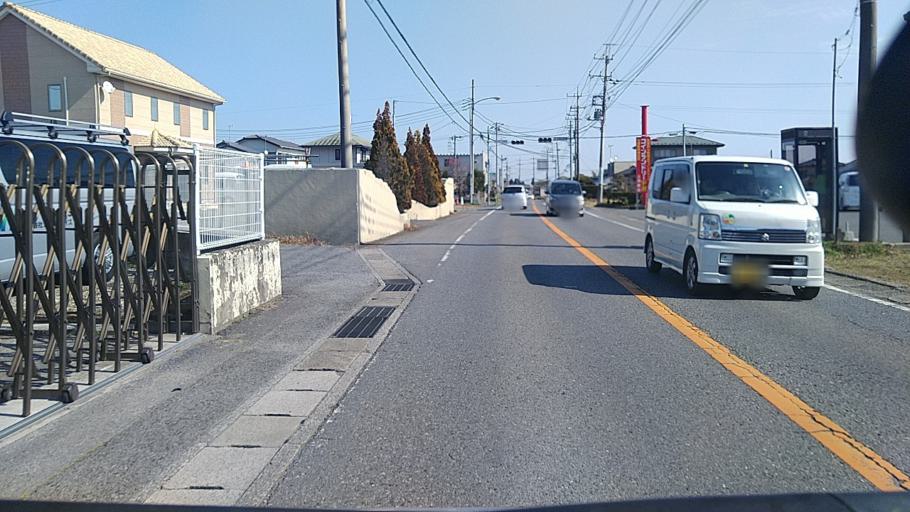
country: JP
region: Chiba
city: Mobara
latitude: 35.4242
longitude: 140.2684
